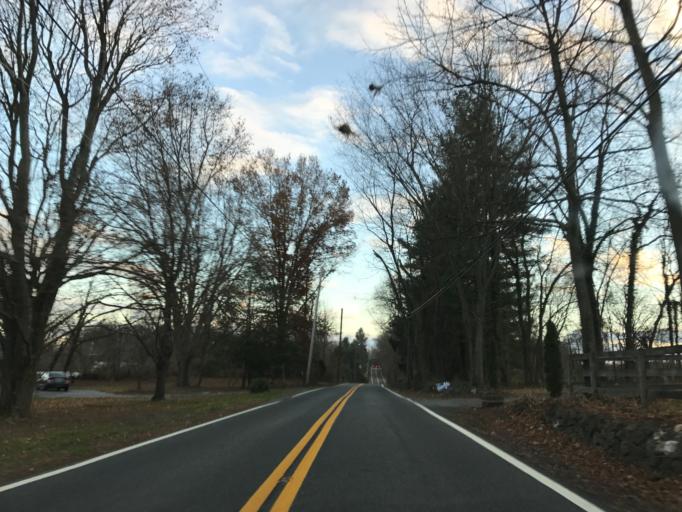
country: US
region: Maryland
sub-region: Cecil County
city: Rising Sun
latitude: 39.6652
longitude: -76.2102
